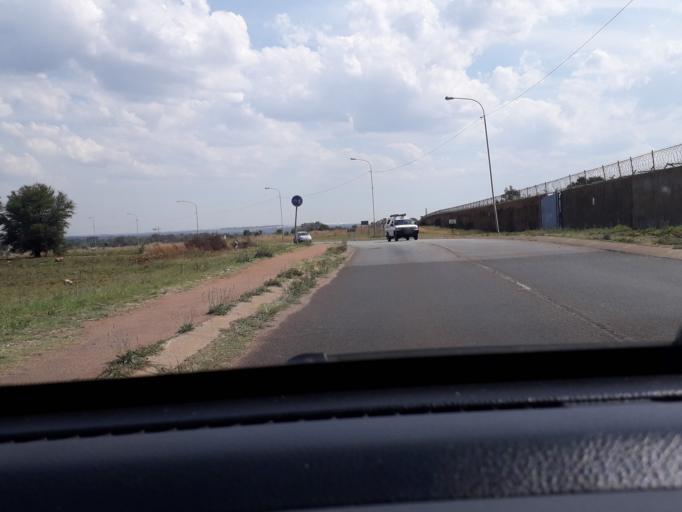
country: ZA
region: Gauteng
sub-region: City of Tshwane Metropolitan Municipality
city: Centurion
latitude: -25.8449
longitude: 28.2275
